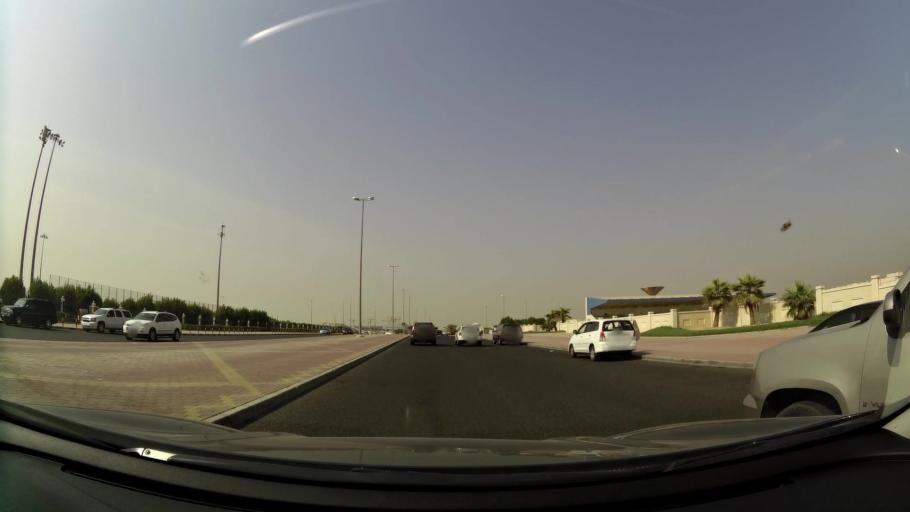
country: KW
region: Al Asimah
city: Ar Rabiyah
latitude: 29.2747
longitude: 47.9179
